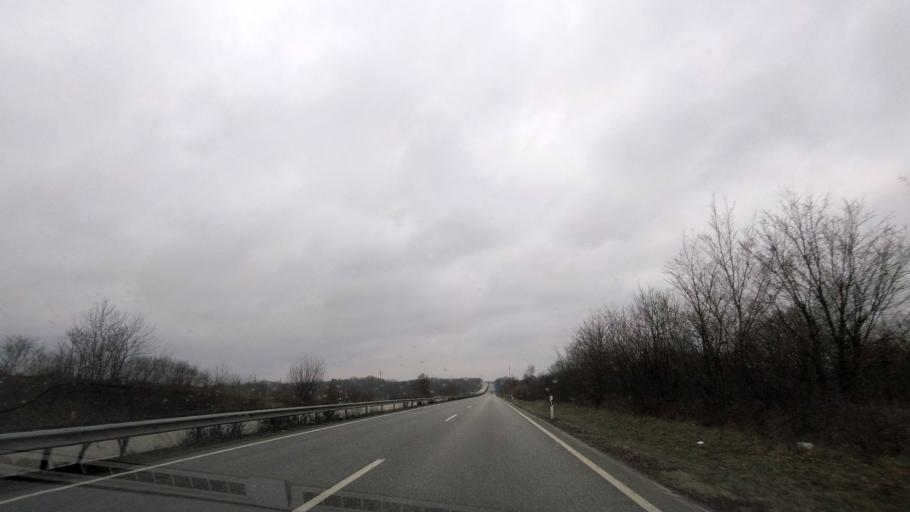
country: DE
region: Schleswig-Holstein
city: Hogersdorf
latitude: 53.9074
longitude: 10.2753
